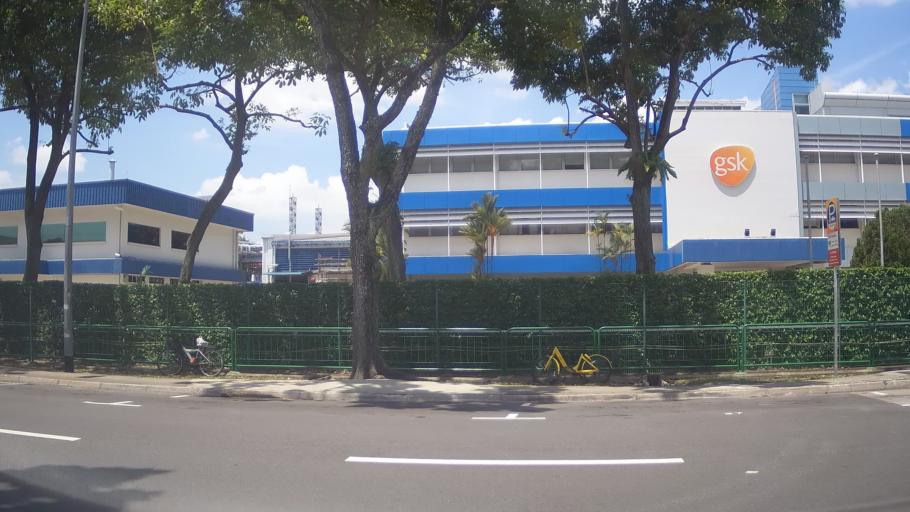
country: MY
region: Johor
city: Johor Bahru
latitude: 1.3348
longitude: 103.7109
